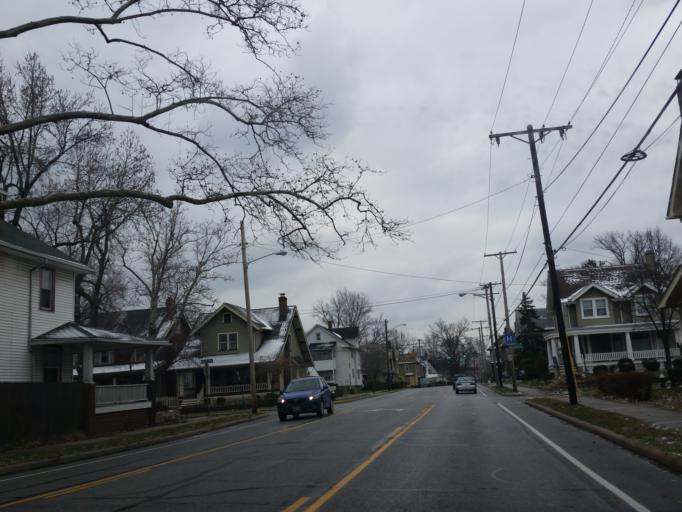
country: US
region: Ohio
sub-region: Cuyahoga County
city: Lakewood
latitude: 41.4818
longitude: -81.7962
